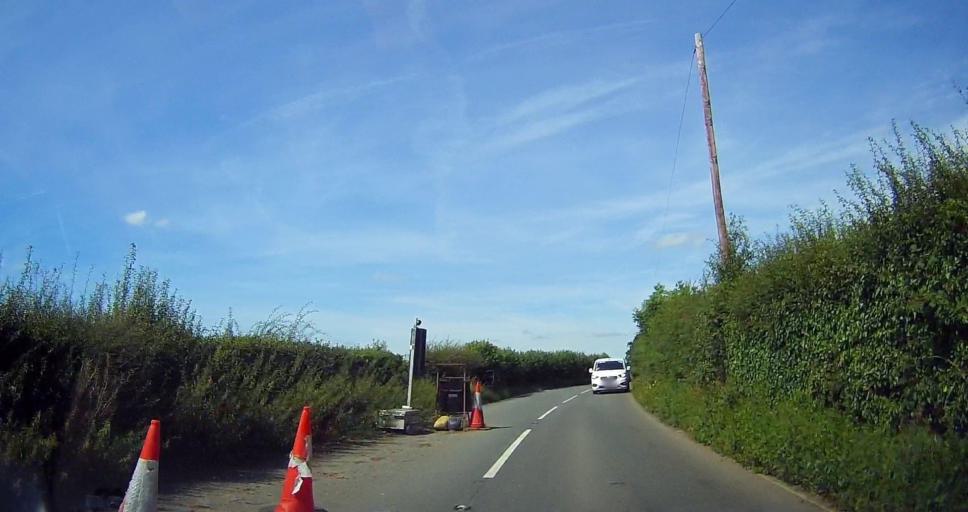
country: GB
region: England
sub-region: Shropshire
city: Market Drayton
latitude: 52.9620
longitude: -2.5155
